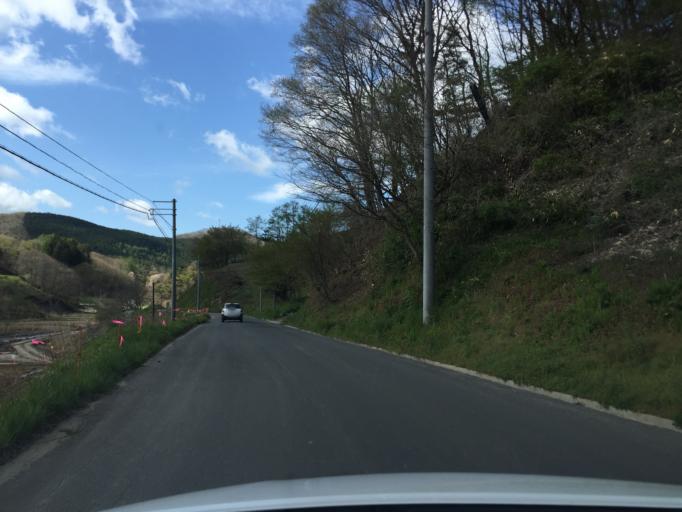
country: JP
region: Fukushima
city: Funehikimachi-funehiki
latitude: 37.5837
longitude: 140.6903
